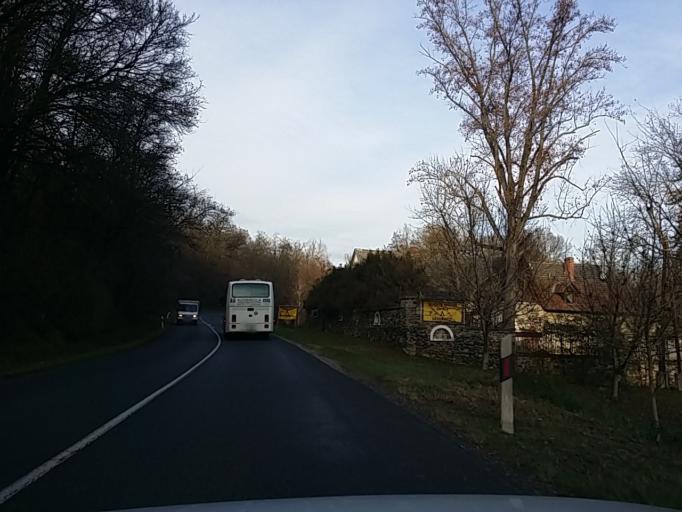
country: HU
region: Veszprem
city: Zanka
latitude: 46.9465
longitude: 17.5935
